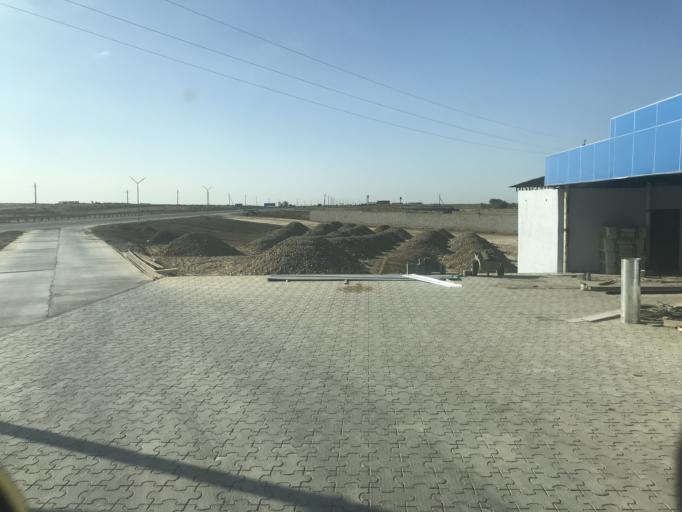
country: KZ
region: Ongtustik Qazaqstan
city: Shymkent
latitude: 42.4576
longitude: 69.6007
